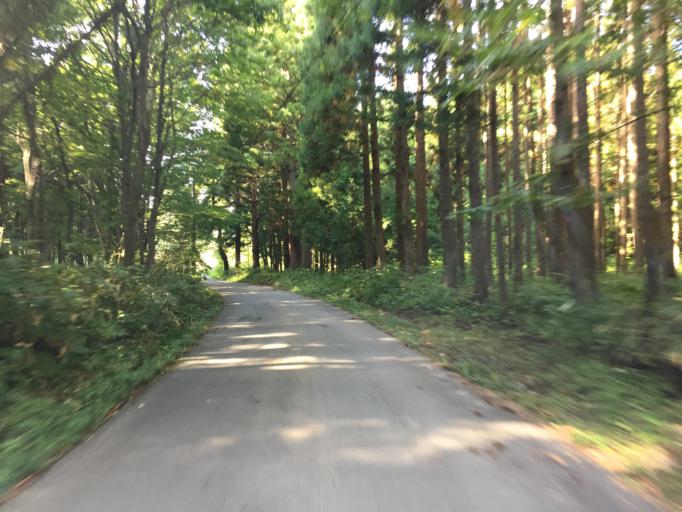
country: JP
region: Yamagata
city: Yonezawa
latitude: 37.8313
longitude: 140.2105
